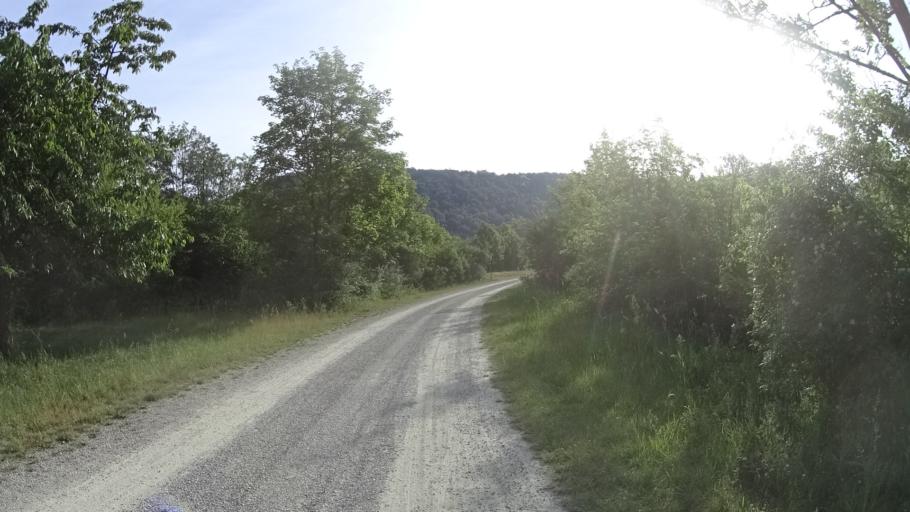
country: DE
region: Bavaria
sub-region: Lower Bavaria
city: Riedenburg
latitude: 48.9916
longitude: 11.6760
